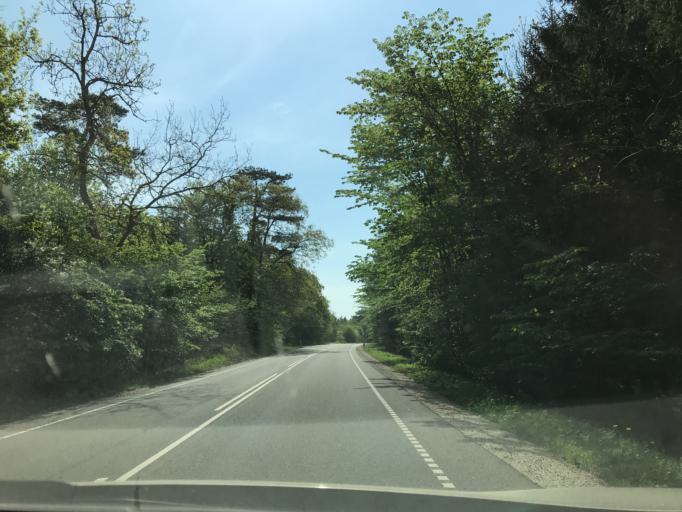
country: DK
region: South Denmark
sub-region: Middelfart Kommune
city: Ejby
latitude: 55.3924
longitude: 9.9114
